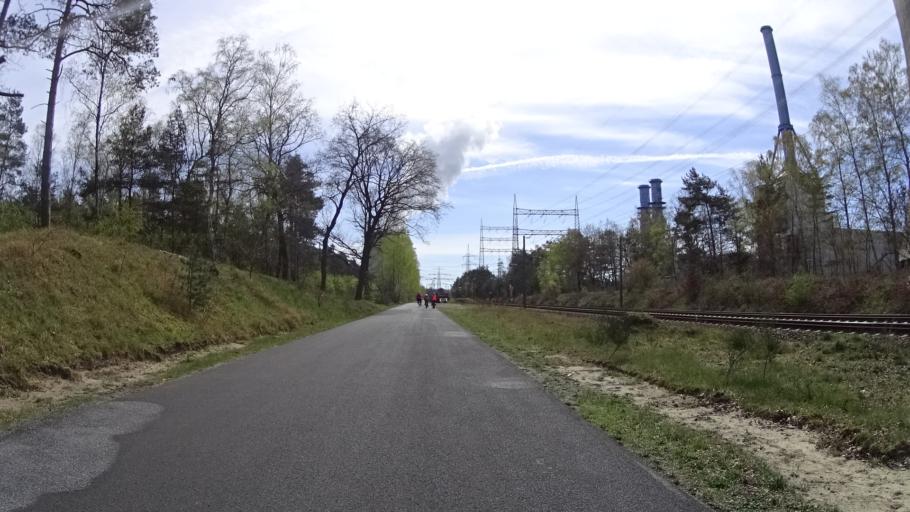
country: DE
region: Lower Saxony
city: Lingen
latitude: 52.4828
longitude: 7.3078
